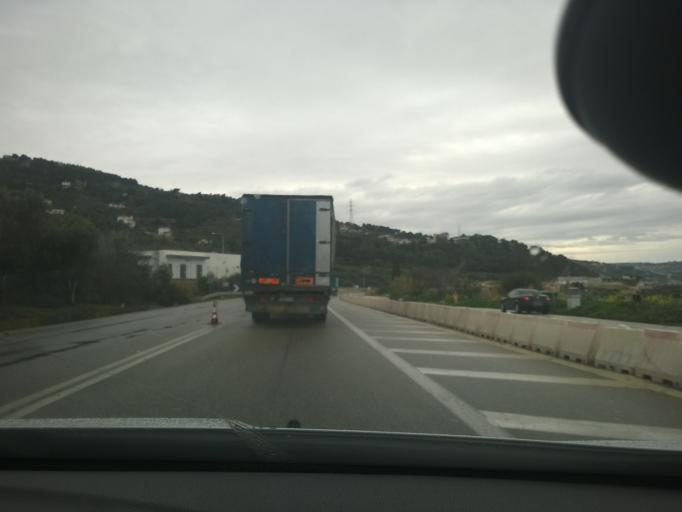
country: GR
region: West Greece
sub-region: Nomos Achaias
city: Aiyira
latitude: 38.1412
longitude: 22.3766
